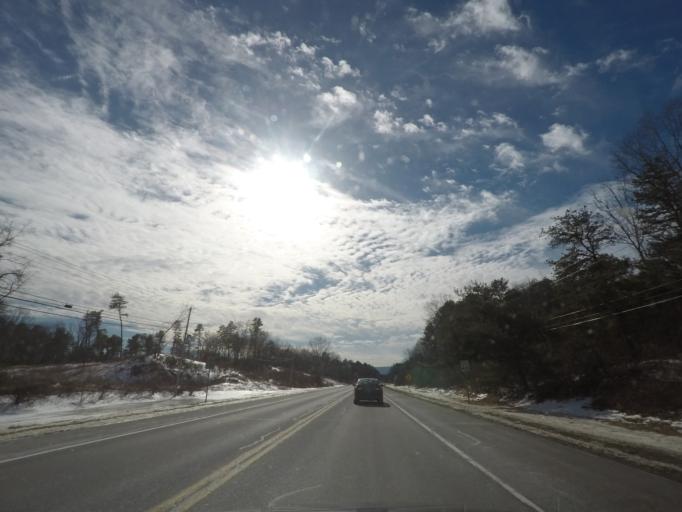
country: US
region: New York
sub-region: Albany County
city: Westmere
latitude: 42.7106
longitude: -73.8739
